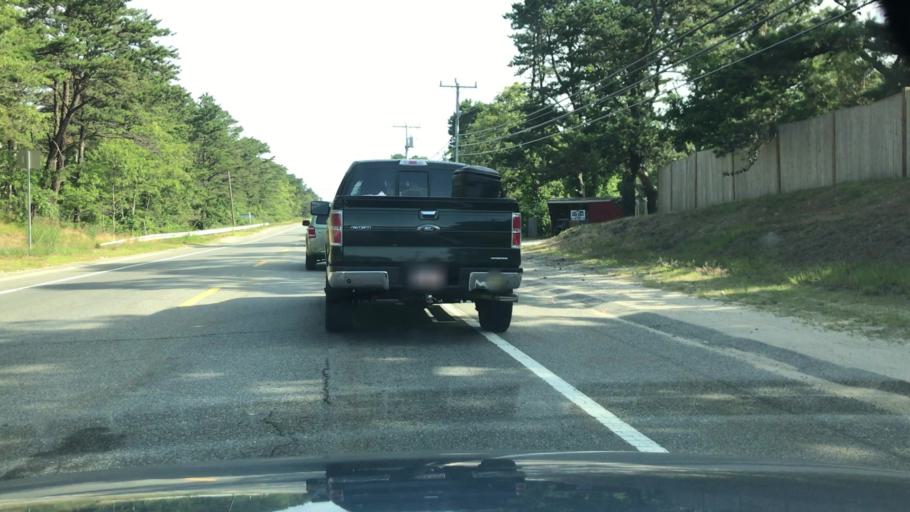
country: US
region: Massachusetts
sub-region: Barnstable County
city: North Eastham
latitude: 41.8806
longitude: -69.9882
